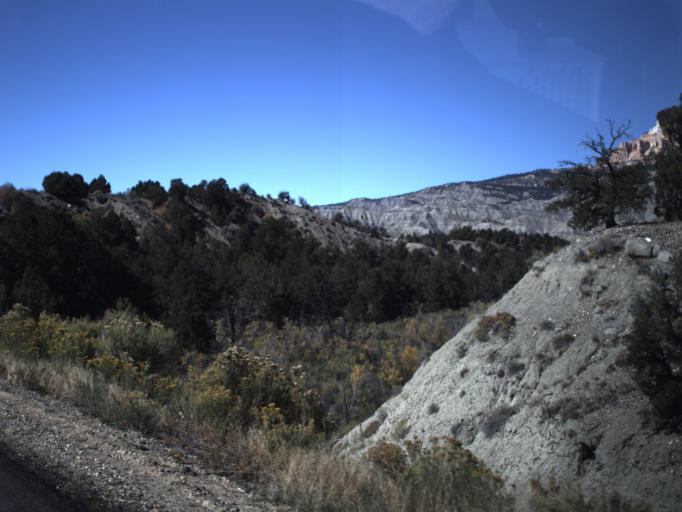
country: US
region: Utah
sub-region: Garfield County
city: Panguitch
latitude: 37.6216
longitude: -111.8645
